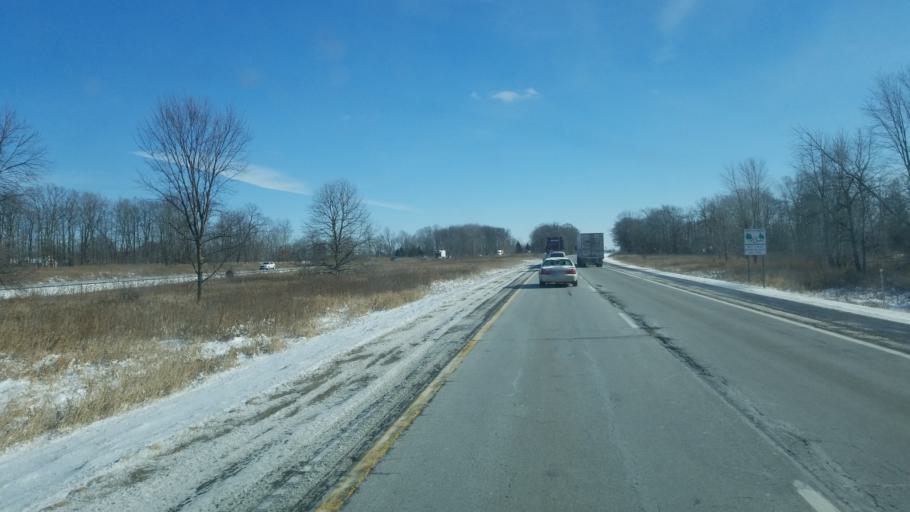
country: US
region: Michigan
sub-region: Livingston County
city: Fowlerville
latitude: 42.6393
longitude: -84.0336
